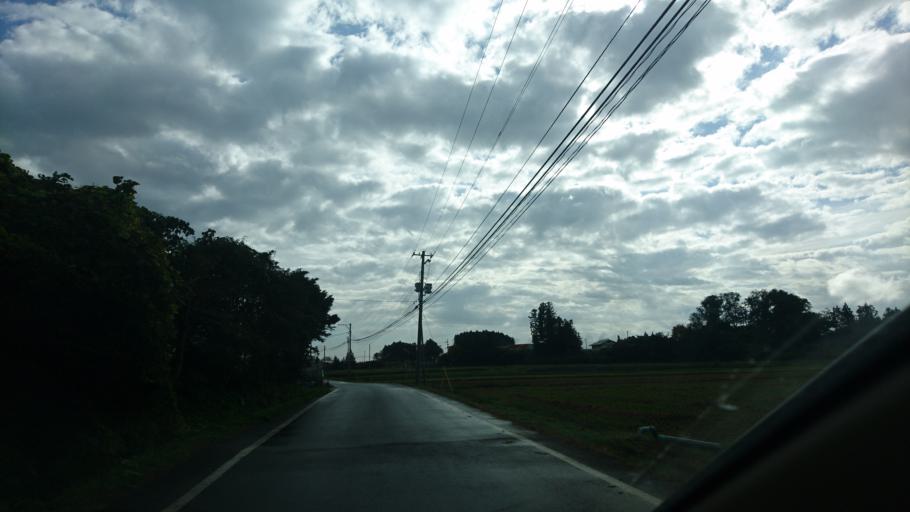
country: JP
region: Iwate
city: Ichinoseki
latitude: 38.7860
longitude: 141.0066
